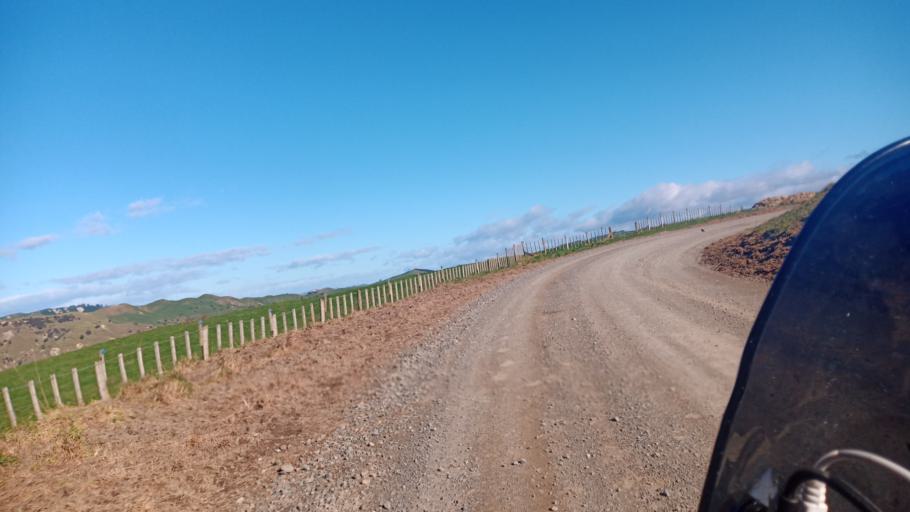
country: NZ
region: Hawke's Bay
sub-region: Wairoa District
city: Wairoa
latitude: -38.7925
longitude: 177.2776
